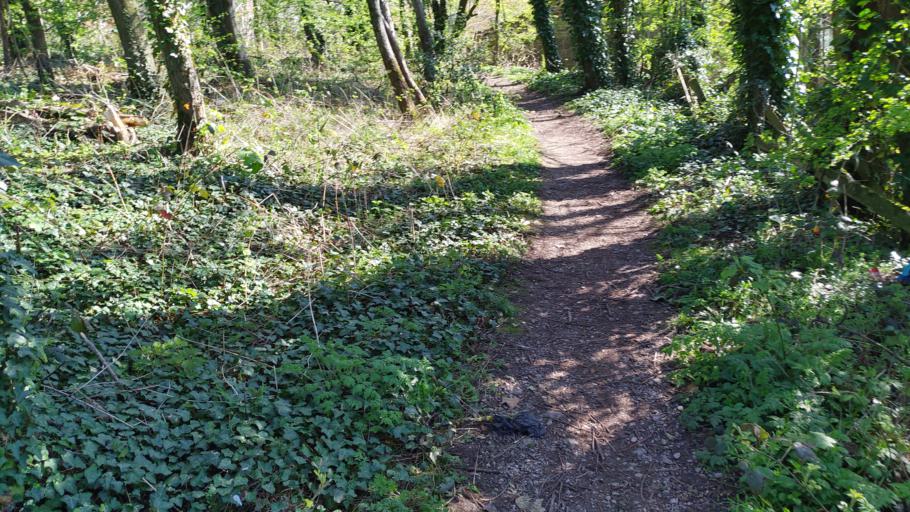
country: GB
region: England
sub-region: Lancashire
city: Chorley
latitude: 53.6805
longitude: -2.6194
